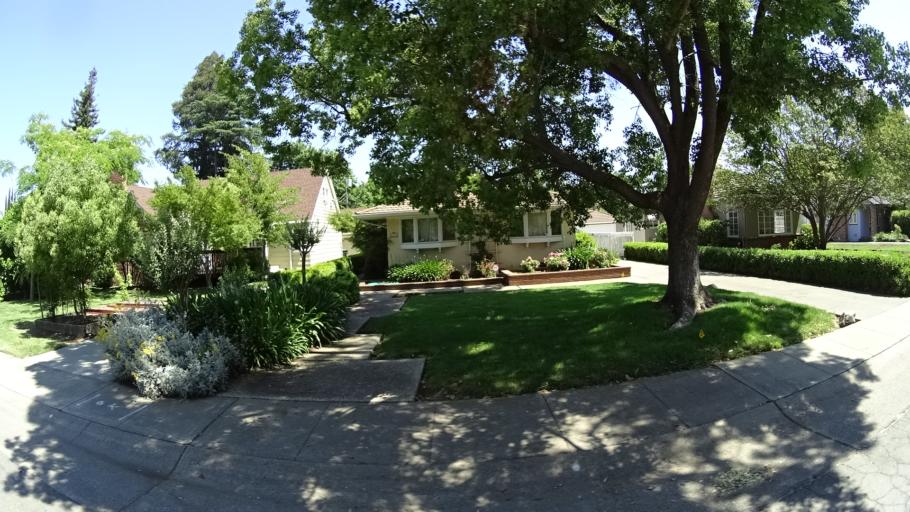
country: US
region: California
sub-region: Sacramento County
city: Sacramento
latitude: 38.5488
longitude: -121.5023
